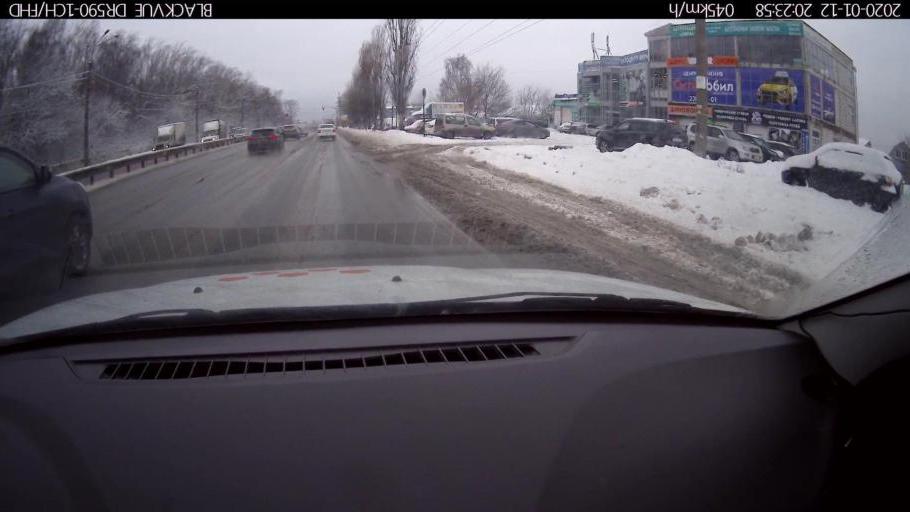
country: RU
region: Nizjnij Novgorod
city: Nizhniy Novgorod
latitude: 56.2878
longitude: 43.8912
